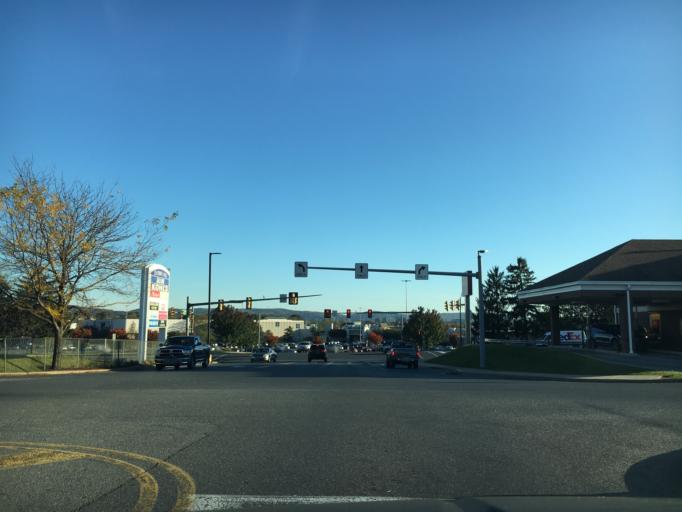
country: US
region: Pennsylvania
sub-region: Lehigh County
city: Fullerton
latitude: 40.6341
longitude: -75.4818
